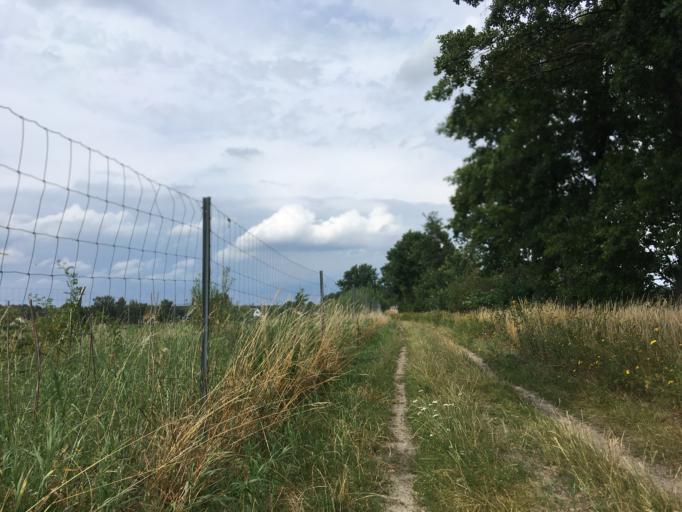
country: DE
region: Brandenburg
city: Bernau bei Berlin
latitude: 52.6328
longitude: 13.5860
